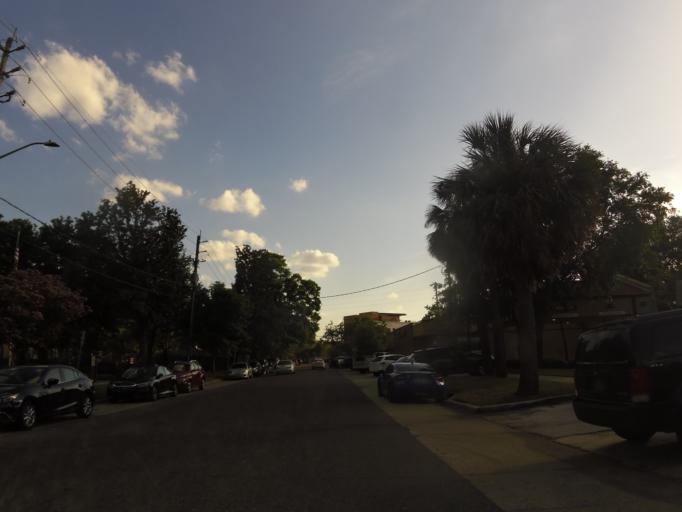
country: US
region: Florida
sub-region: Duval County
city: Jacksonville
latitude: 30.3143
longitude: -81.6799
